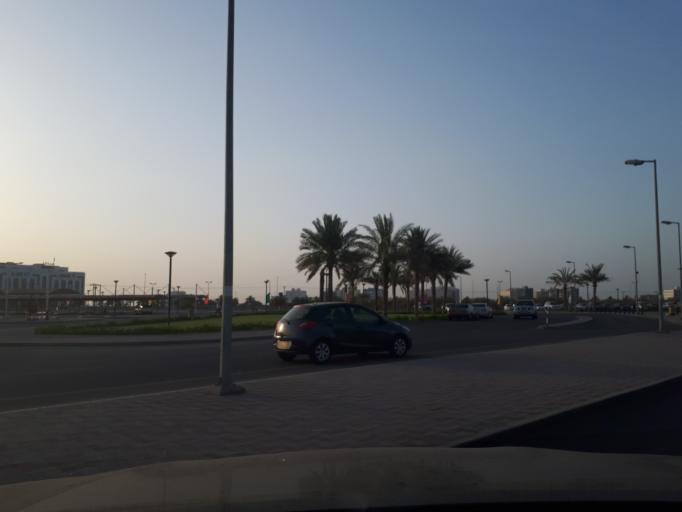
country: OM
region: Muhafazat Masqat
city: As Sib al Jadidah
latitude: 23.5850
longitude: 58.2005
